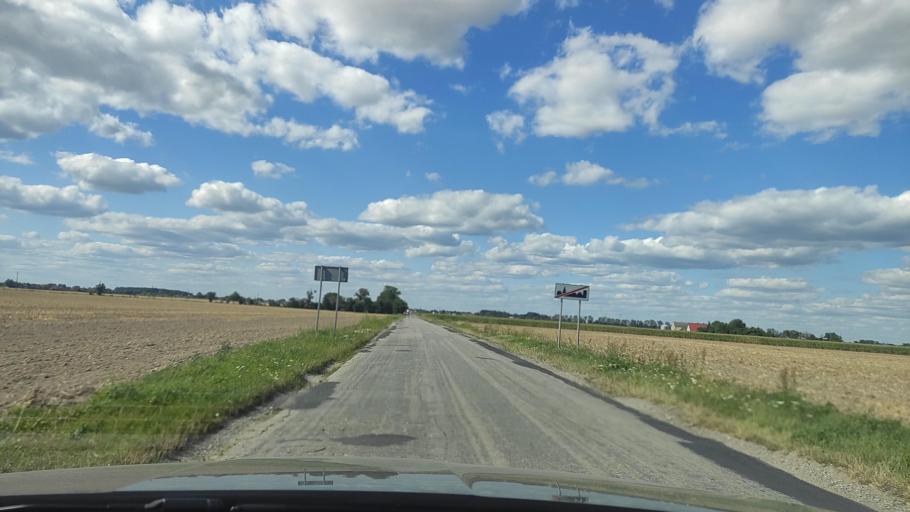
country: PL
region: Greater Poland Voivodeship
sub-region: Powiat poznanski
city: Kleszczewo
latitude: 52.3581
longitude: 17.1712
